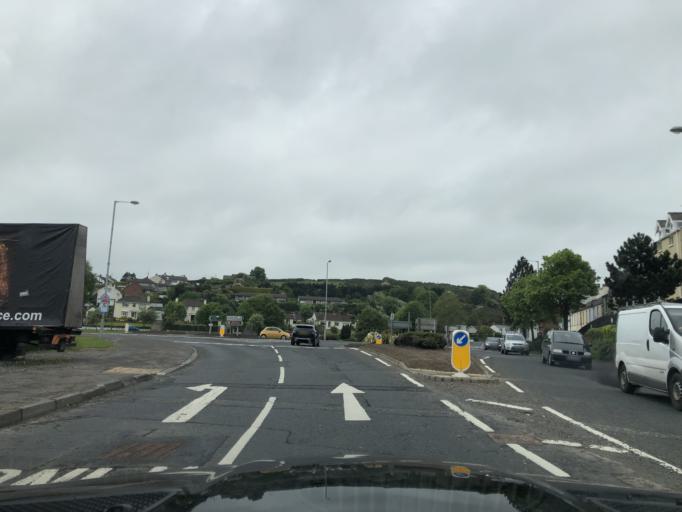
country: GB
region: Northern Ireland
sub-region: Down District
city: Downpatrick
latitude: 54.3339
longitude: -5.7166
